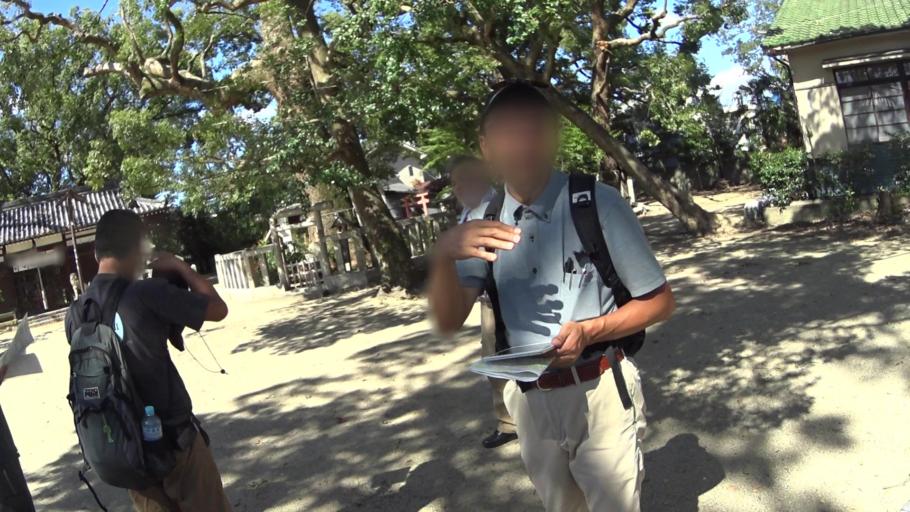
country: JP
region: Osaka
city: Yao
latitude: 34.6316
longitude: 135.5584
